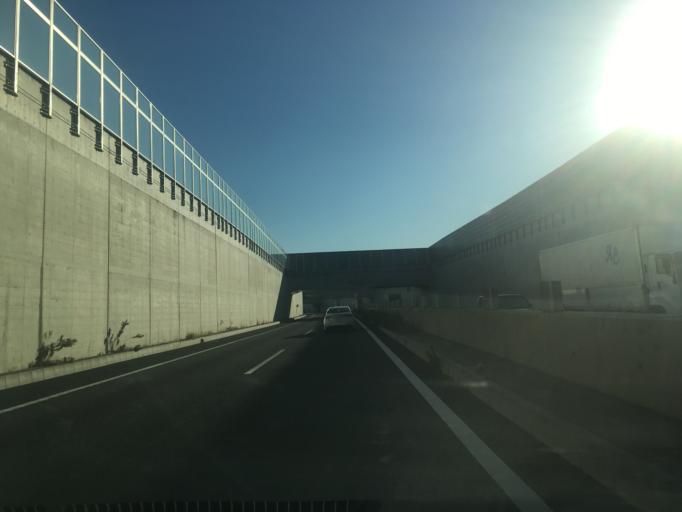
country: JP
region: Saitama
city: Okegawa
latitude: 36.0108
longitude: 139.5417
